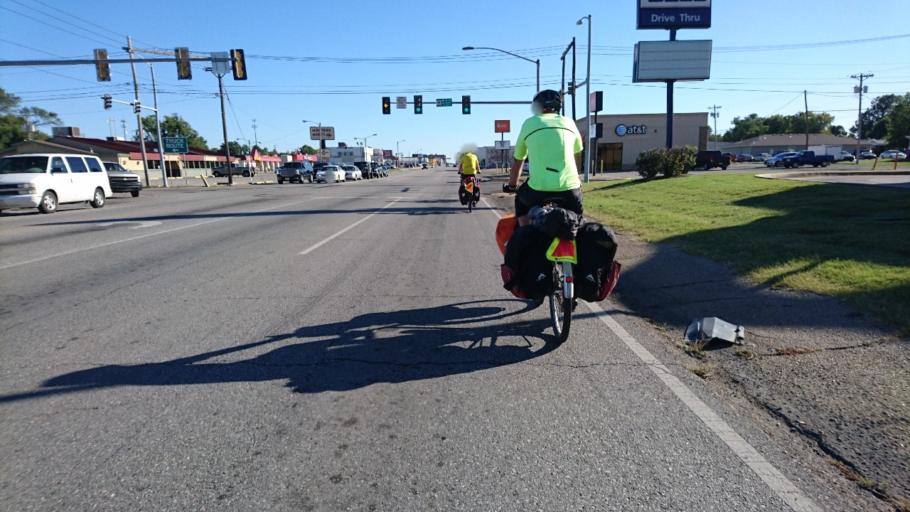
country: US
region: Oklahoma
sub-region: Ottawa County
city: Miami
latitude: 36.8858
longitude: -94.8776
